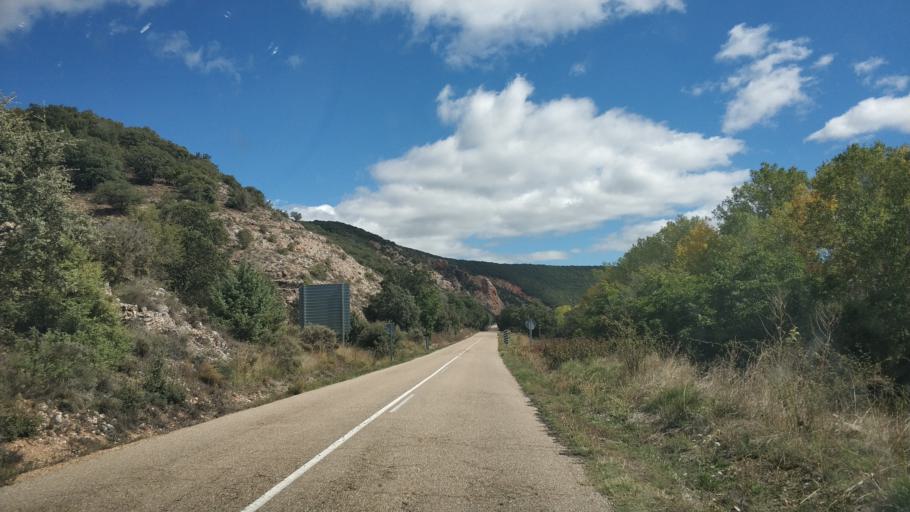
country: ES
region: Castille and Leon
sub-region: Provincia de Burgos
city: Covarrubias
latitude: 42.0534
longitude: -3.5047
